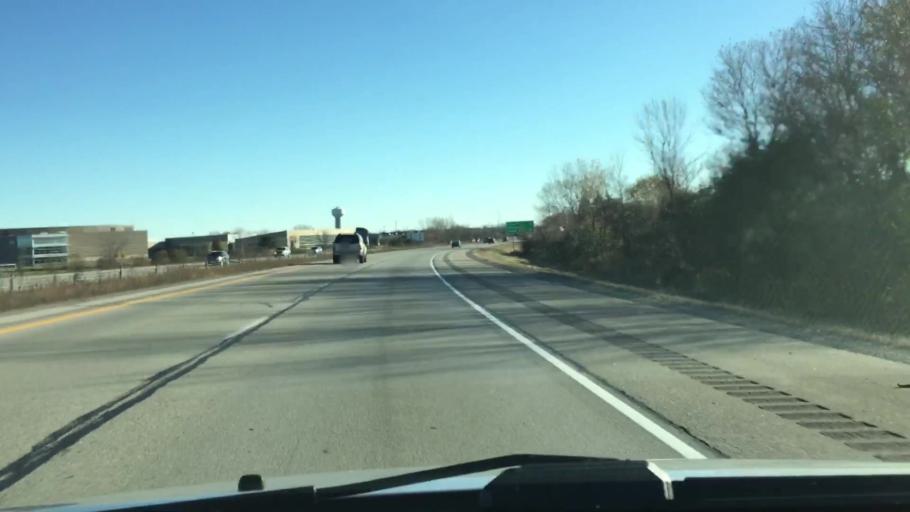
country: US
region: Wisconsin
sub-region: Outagamie County
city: Appleton
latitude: 44.2987
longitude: -88.4550
